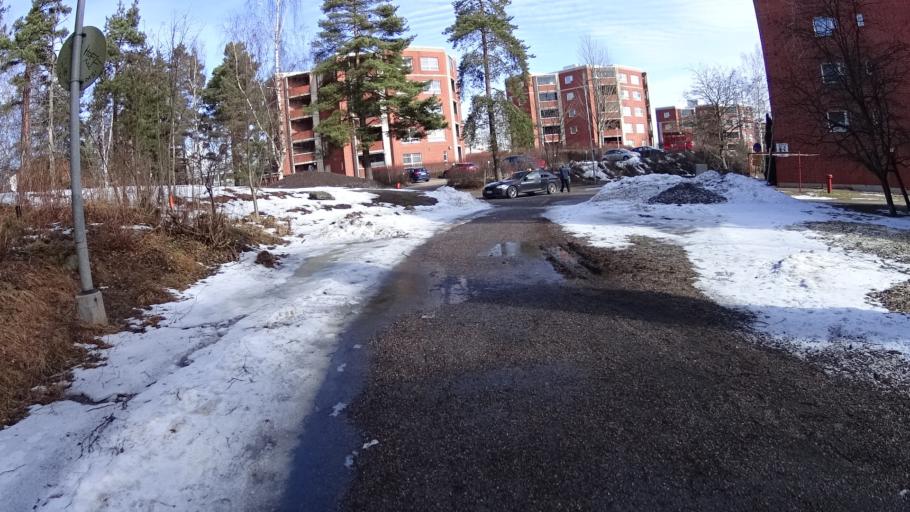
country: FI
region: Uusimaa
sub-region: Helsinki
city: Kilo
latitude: 60.2260
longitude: 24.8199
